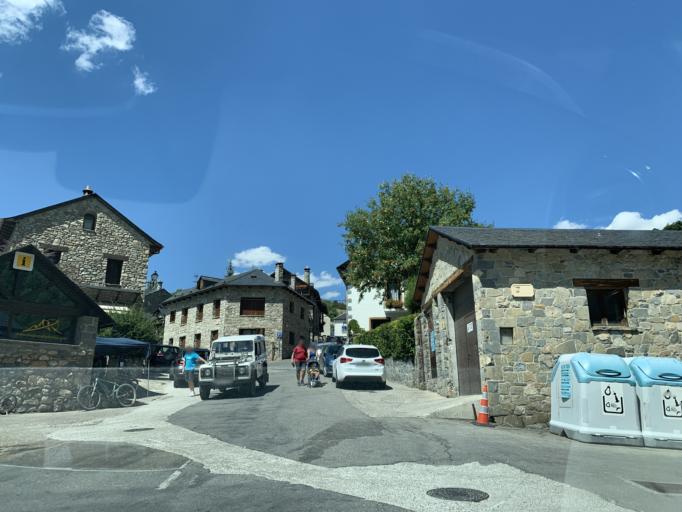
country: ES
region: Aragon
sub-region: Provincia de Huesca
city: Hoz de Jaca
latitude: 42.6897
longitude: -0.3055
